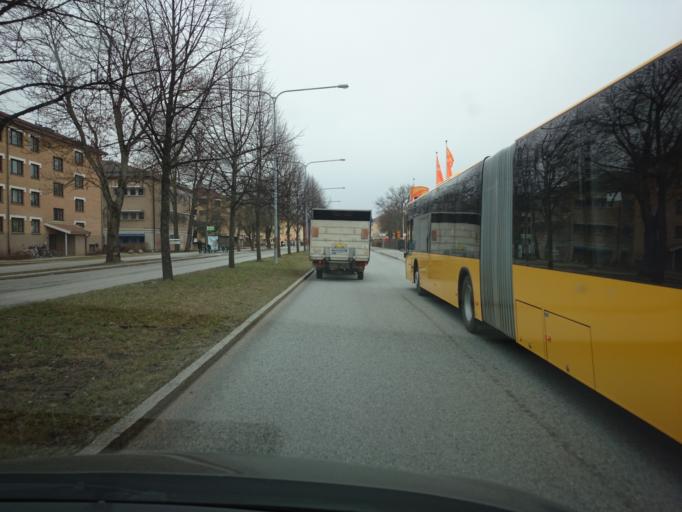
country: SE
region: Uppsala
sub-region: Uppsala Kommun
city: Uppsala
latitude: 59.8686
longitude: 17.6286
